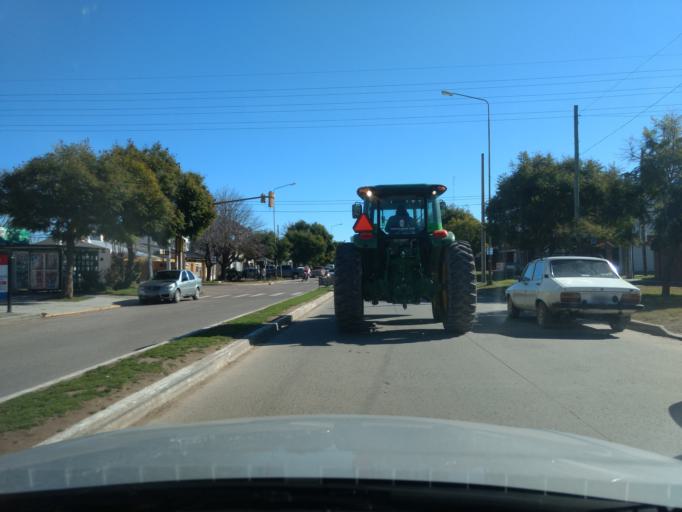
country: AR
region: Buenos Aires
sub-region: Partido de Lujan
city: Lujan
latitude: -34.5806
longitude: -59.1038
